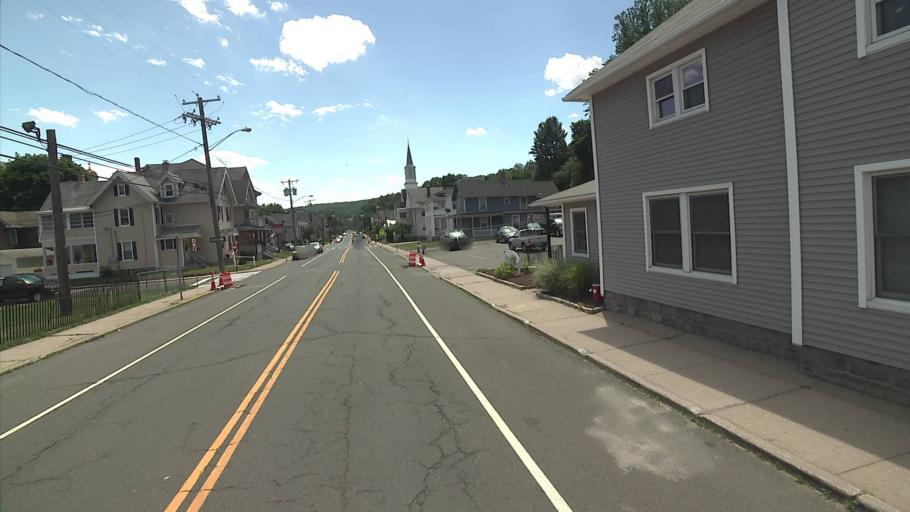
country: US
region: Connecticut
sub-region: New Haven County
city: Naugatuck
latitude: 41.4941
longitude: -73.0557
